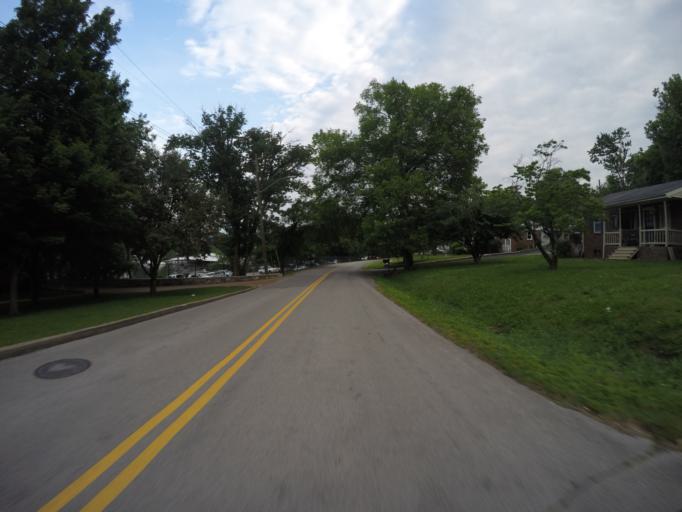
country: US
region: Tennessee
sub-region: Davidson County
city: Lakewood
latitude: 36.2534
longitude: -86.6407
